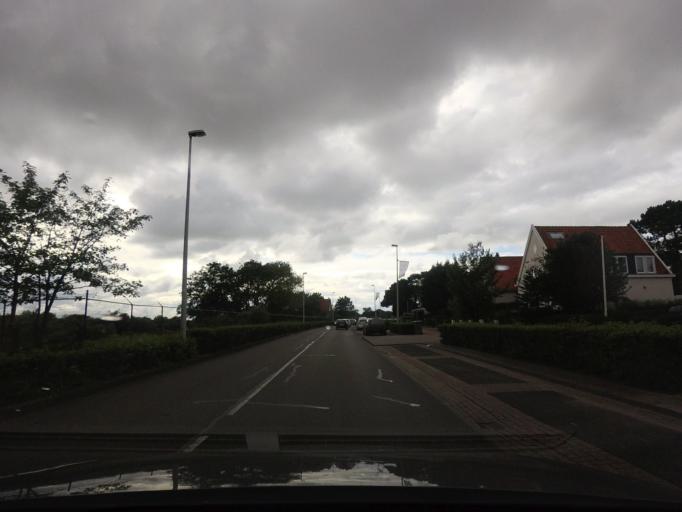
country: NL
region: North Holland
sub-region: Gemeente Zandvoort
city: Zandvoort
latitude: 52.3651
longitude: 4.5522
